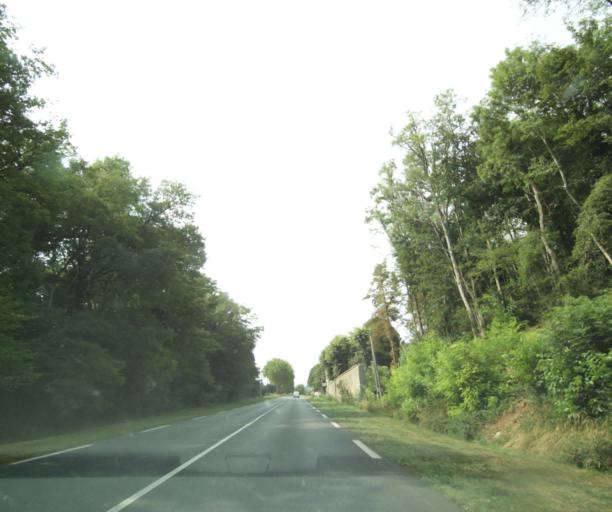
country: FR
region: Centre
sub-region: Departement d'Indre-et-Loire
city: La Membrolle-sur-Choisille
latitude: 47.4438
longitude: 0.6356
